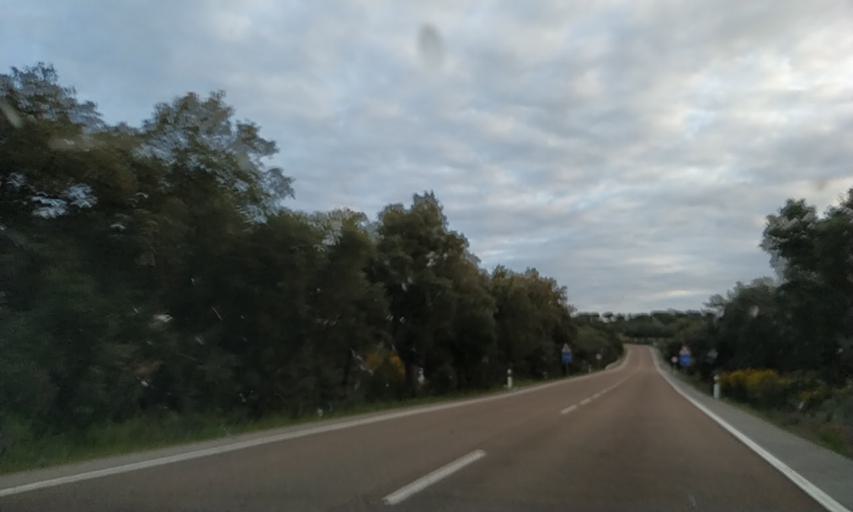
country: ES
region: Extremadura
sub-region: Provincia de Badajoz
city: Puebla de Obando
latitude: 39.2499
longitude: -6.5570
